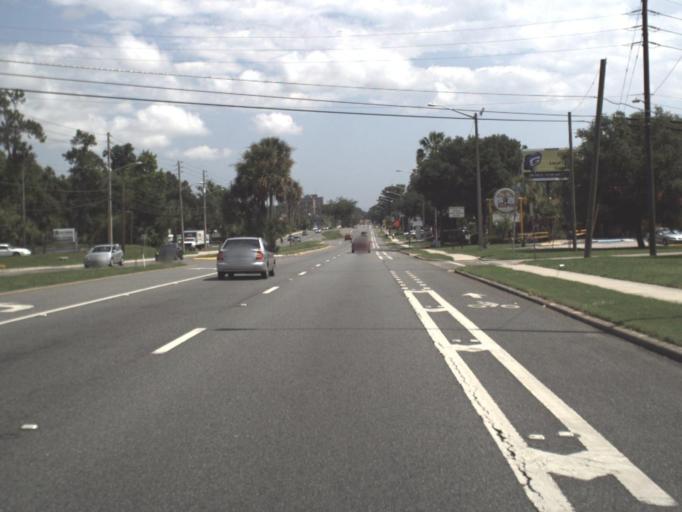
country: US
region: Florida
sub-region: Alachua County
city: Gainesville
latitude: 29.6281
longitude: -82.3392
